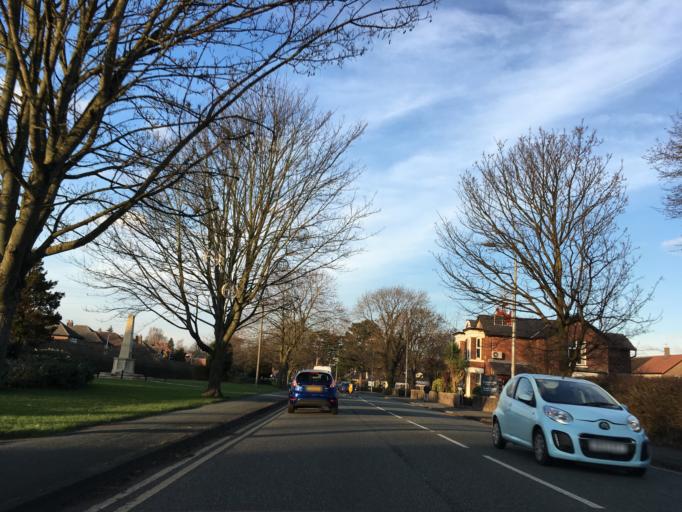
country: GB
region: England
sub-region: Cheshire East
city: Wilmslow
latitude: 53.3512
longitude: -2.2156
